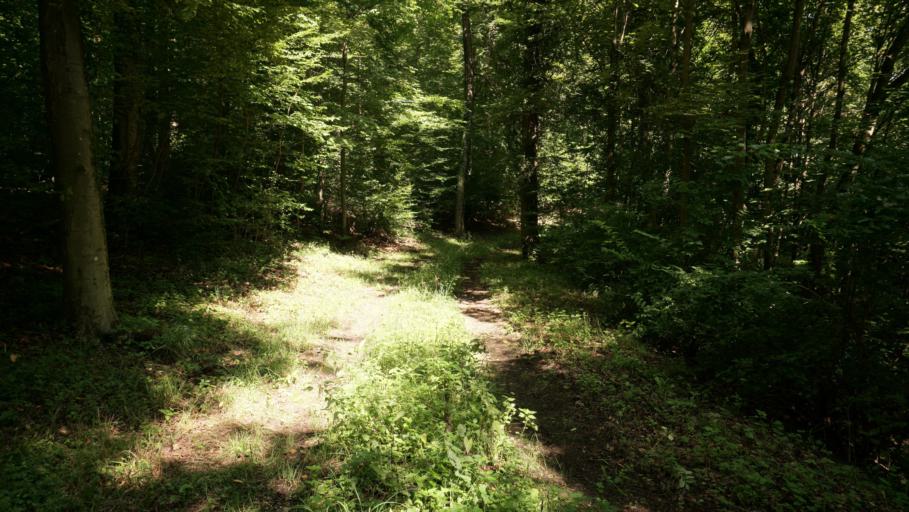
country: DE
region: Baden-Wuerttemberg
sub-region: Karlsruhe Region
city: Neckarzimmern
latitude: 49.3265
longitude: 9.1314
